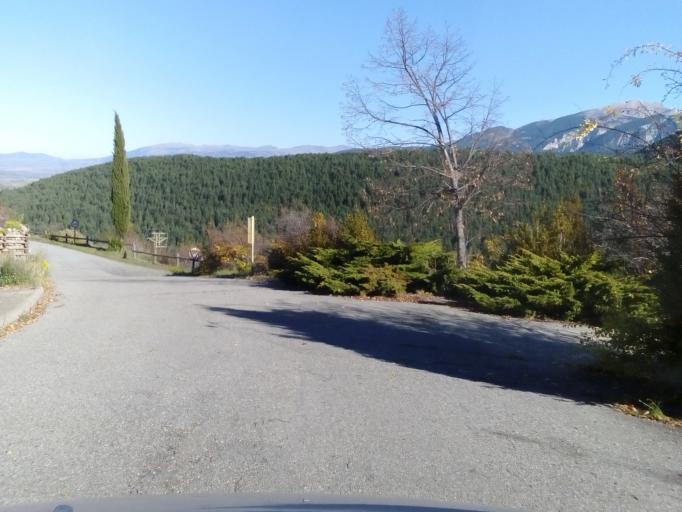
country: ES
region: Catalonia
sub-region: Provincia de Lleida
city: Bellver de Cerdanya
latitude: 42.3413
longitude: 1.7769
